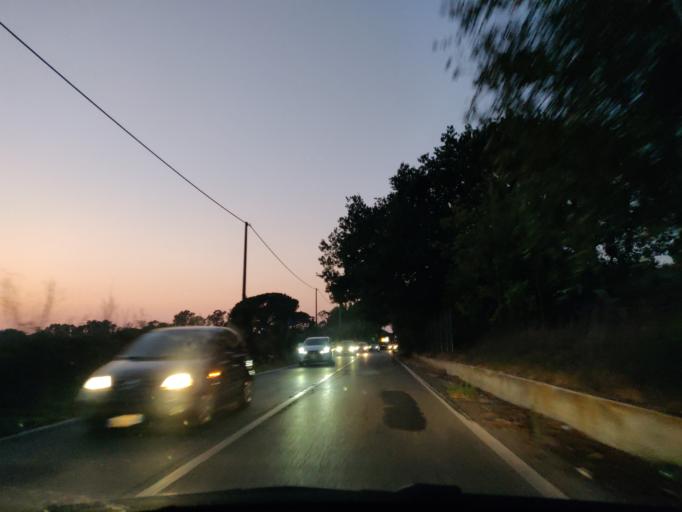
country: IT
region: Latium
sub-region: Citta metropolitana di Roma Capitale
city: Npp 23 (Parco Leonardo)
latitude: 41.8372
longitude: 12.2796
